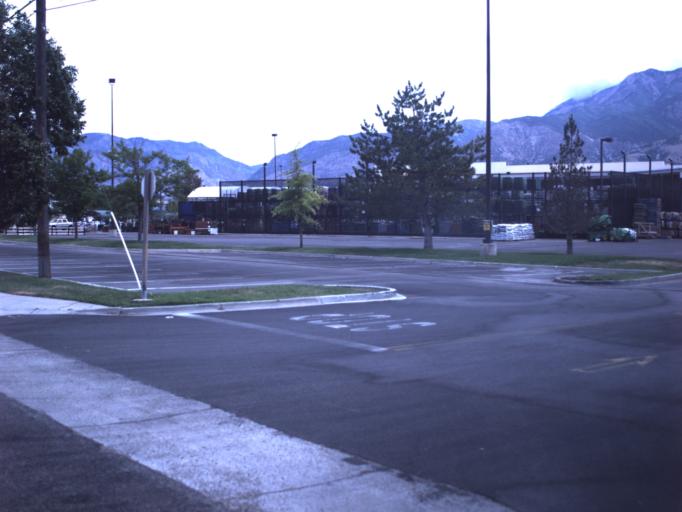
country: US
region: Utah
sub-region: Weber County
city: Riverdale
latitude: 41.1749
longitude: -112.0044
